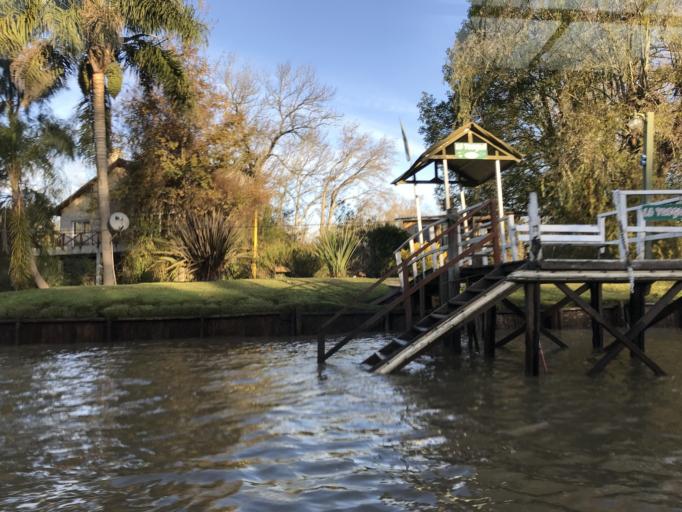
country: AR
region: Buenos Aires
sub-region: Partido de Tigre
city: Tigre
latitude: -34.3724
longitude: -58.5834
